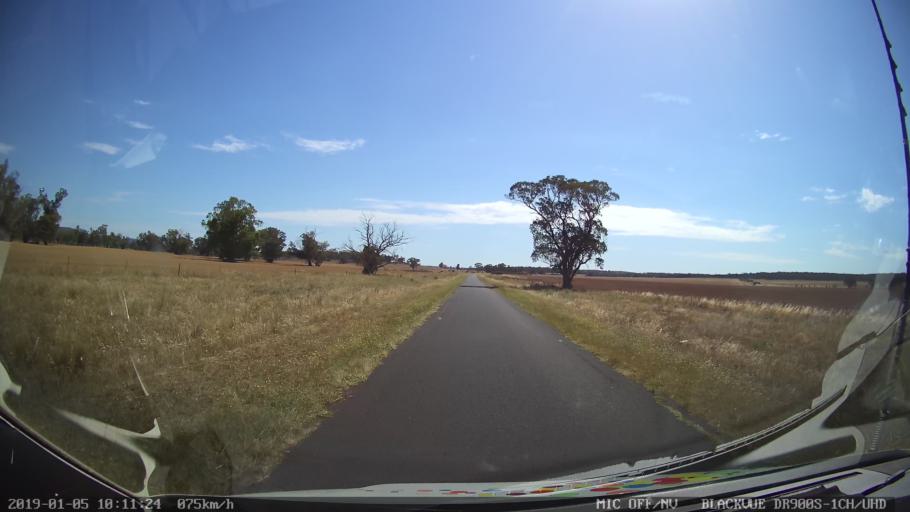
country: AU
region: New South Wales
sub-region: Gilgandra
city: Gilgandra
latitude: -31.6136
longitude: 148.9009
